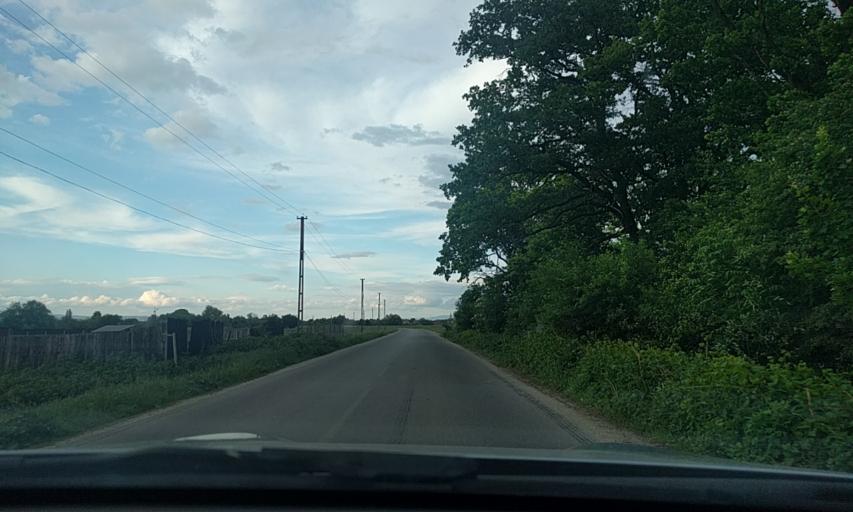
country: RO
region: Brasov
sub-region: Comuna Harman
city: Harman
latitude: 45.7499
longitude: 25.7072
